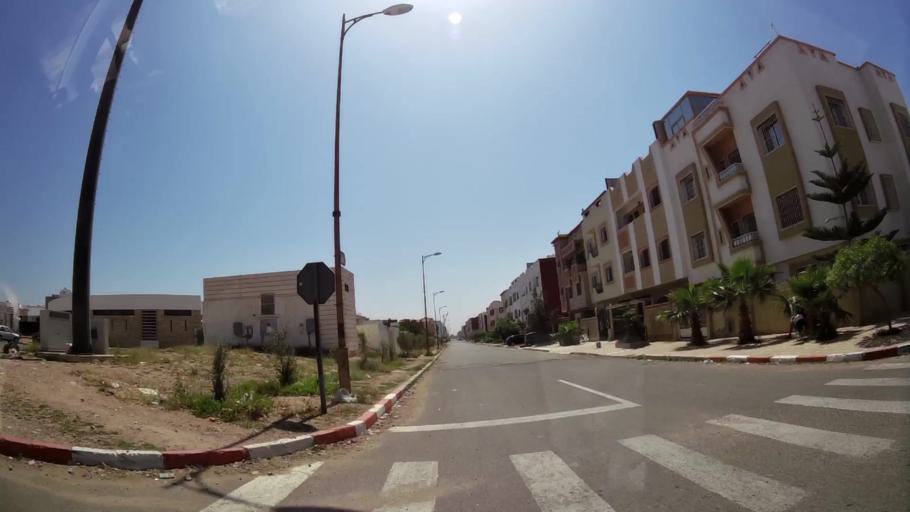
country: MA
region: Oued ed Dahab-Lagouira
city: Dakhla
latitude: 30.4307
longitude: -9.5611
